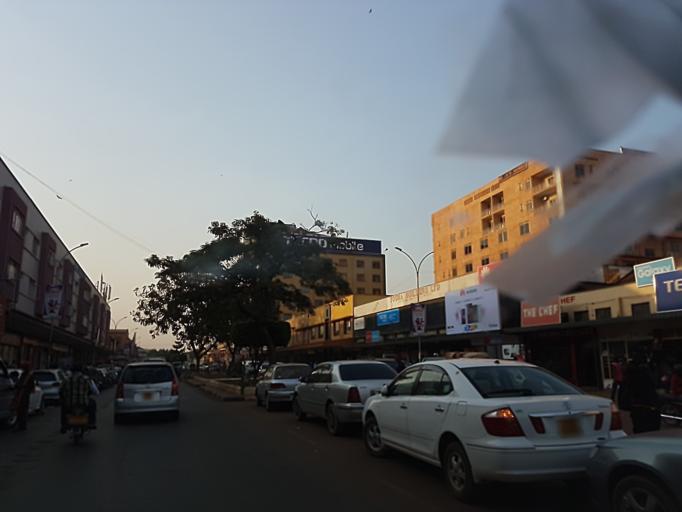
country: UG
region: Central Region
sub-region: Kampala District
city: Kampala
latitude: 0.3162
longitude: 32.5764
